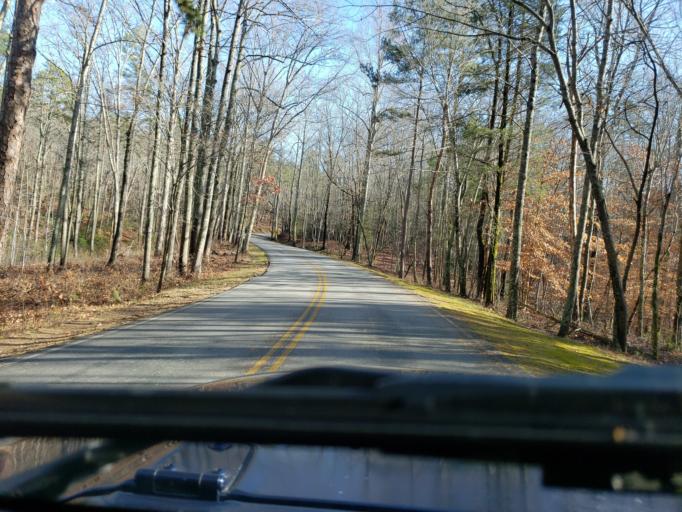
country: US
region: North Carolina
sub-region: Cleveland County
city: White Plains
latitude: 35.1506
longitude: -81.3925
